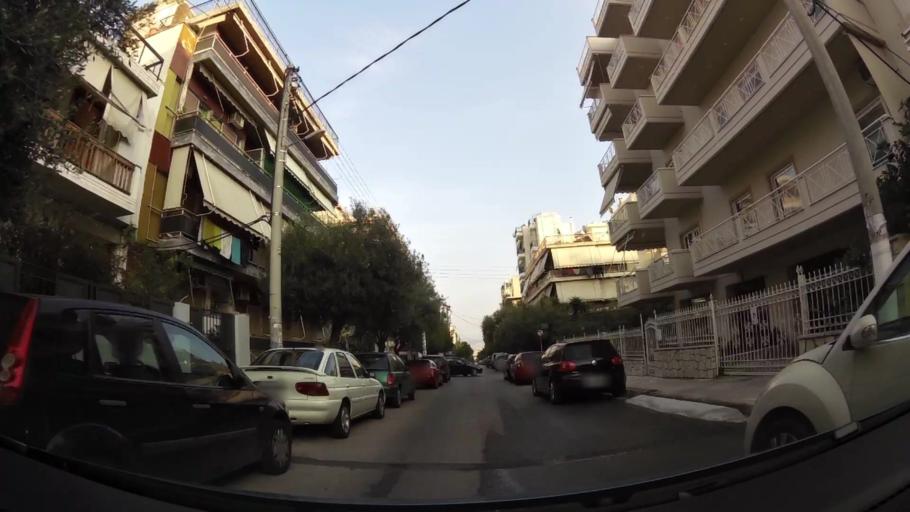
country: GR
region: Attica
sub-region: Nomarchia Athinas
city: Petroupolis
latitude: 38.0399
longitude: 23.6831
